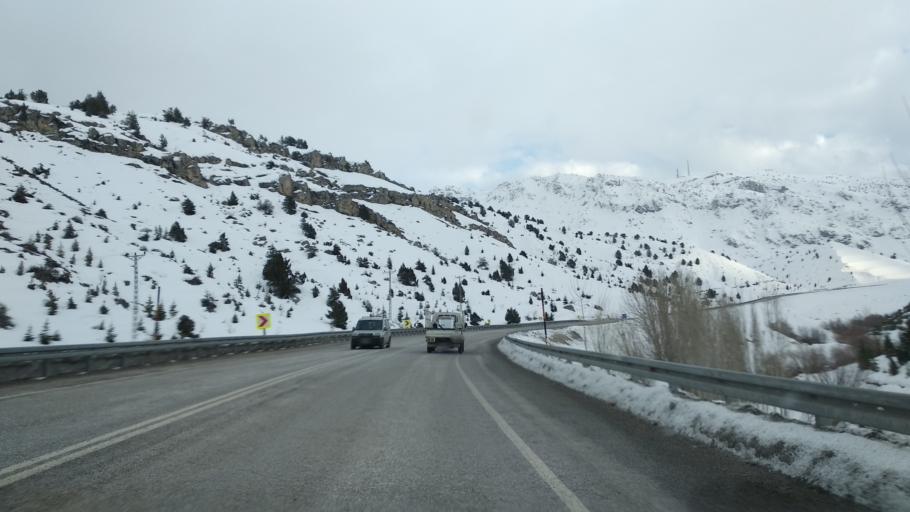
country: TR
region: Kahramanmaras
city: Goksun
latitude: 37.9987
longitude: 36.5373
